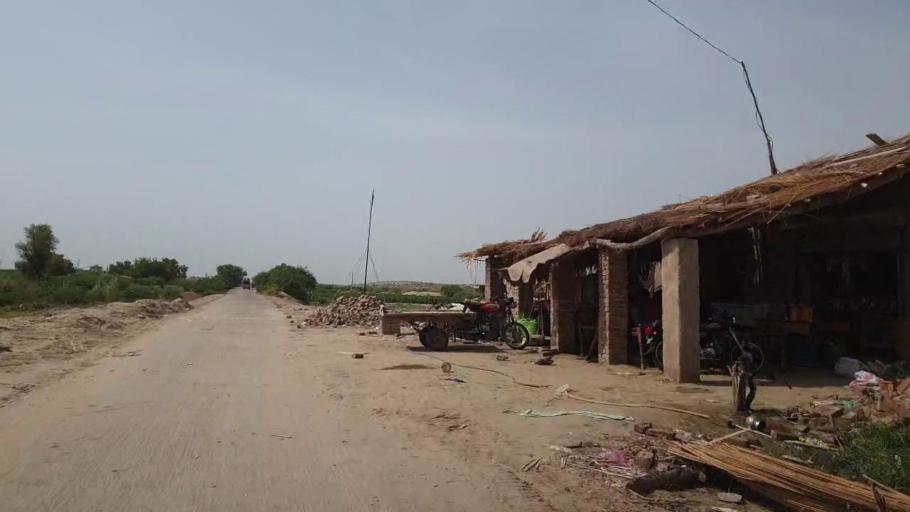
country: PK
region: Sindh
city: Bandhi
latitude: 26.5519
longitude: 68.3839
